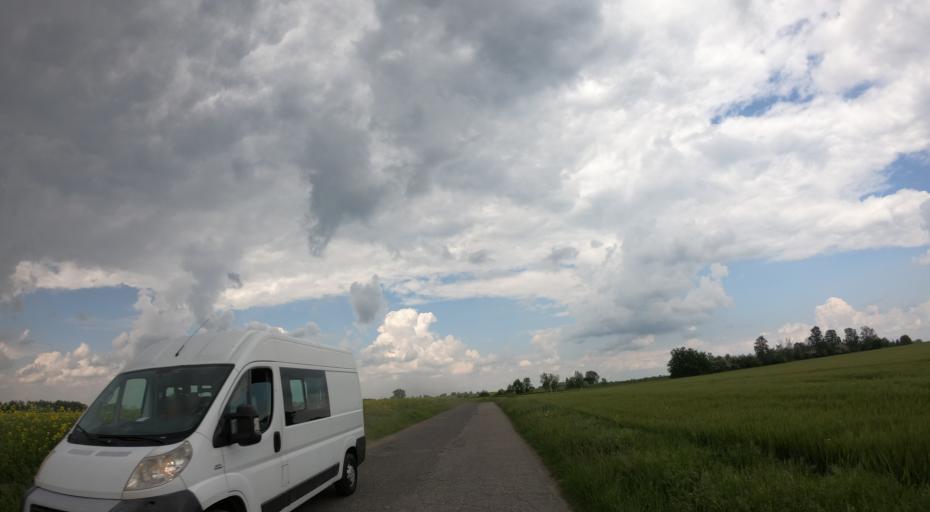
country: PL
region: West Pomeranian Voivodeship
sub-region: Powiat pyrzycki
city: Kozielice
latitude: 53.1587
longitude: 14.7978
